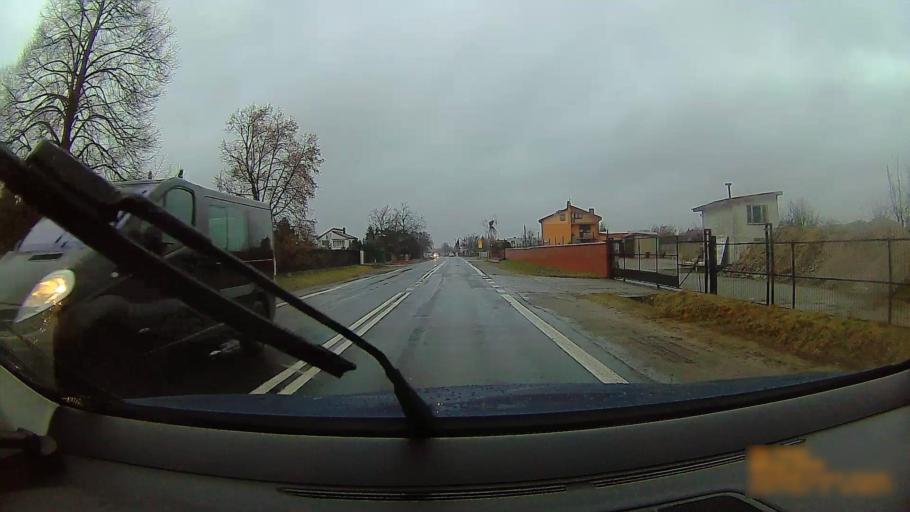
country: PL
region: Greater Poland Voivodeship
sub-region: Konin
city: Konin
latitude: 52.1860
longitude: 18.2676
